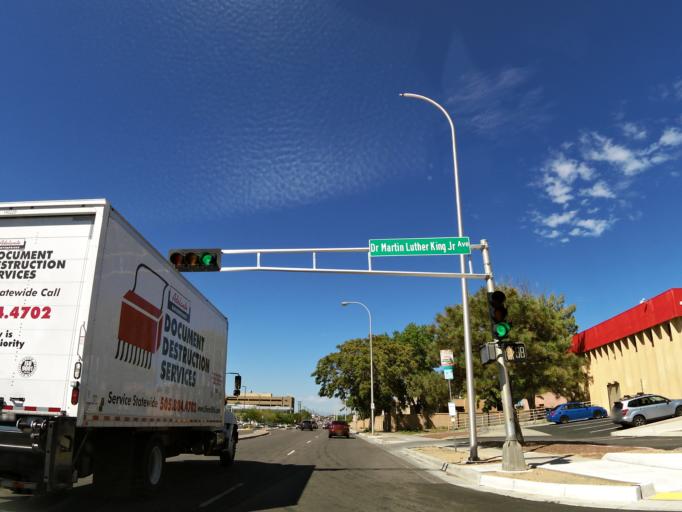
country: US
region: New Mexico
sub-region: Bernalillo County
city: Albuquerque
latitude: 35.0864
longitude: -106.6440
